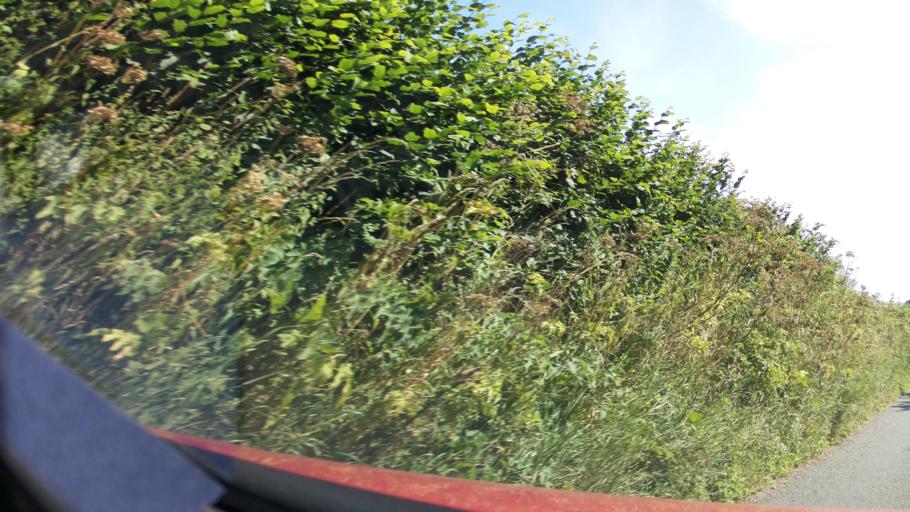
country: GB
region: England
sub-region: West Berkshire
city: Farnborough
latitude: 51.4913
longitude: -1.3658
